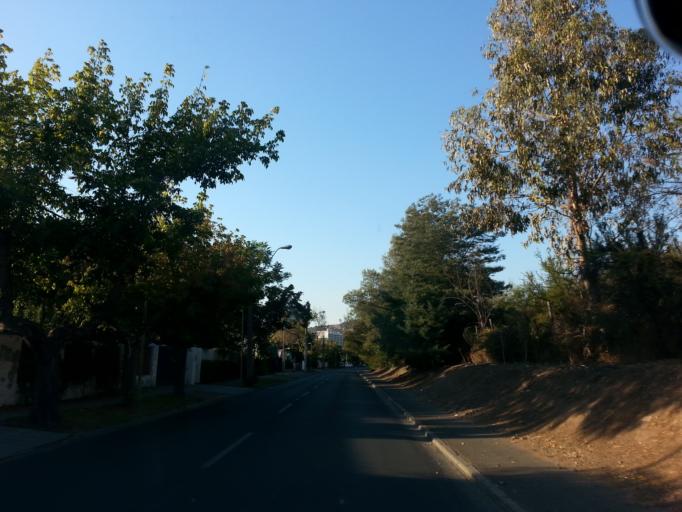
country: CL
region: Santiago Metropolitan
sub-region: Provincia de Santiago
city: Villa Presidente Frei, Nunoa, Santiago, Chile
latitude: -33.3965
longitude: -70.5400
